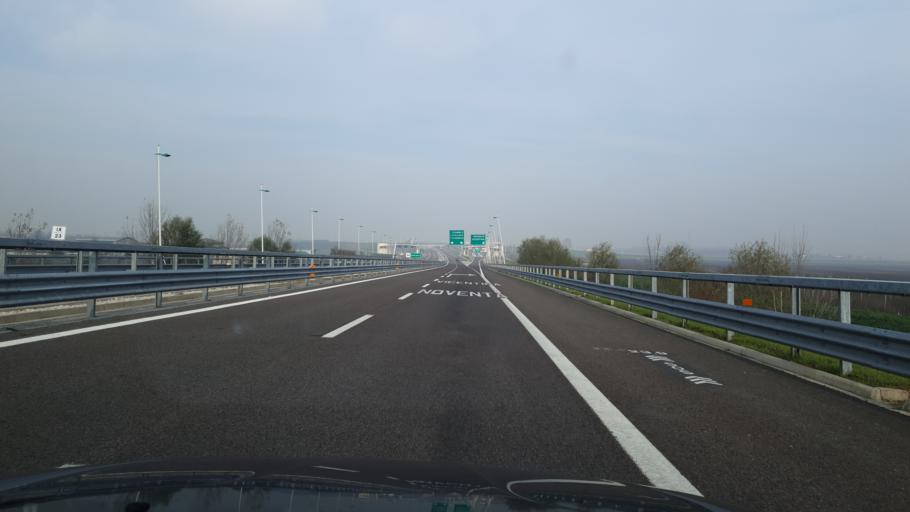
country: IT
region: Veneto
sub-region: Provincia di Vicenza
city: Noventa Vicentina
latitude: 45.2645
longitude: 11.5713
